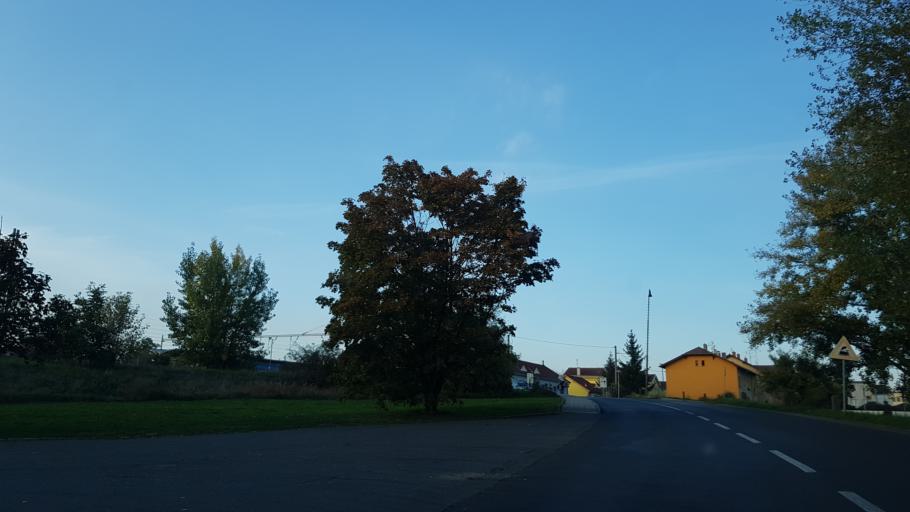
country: CZ
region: Zlin
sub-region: Okres Uherske Hradiste
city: Stare Mesto
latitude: 49.0742
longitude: 17.4222
